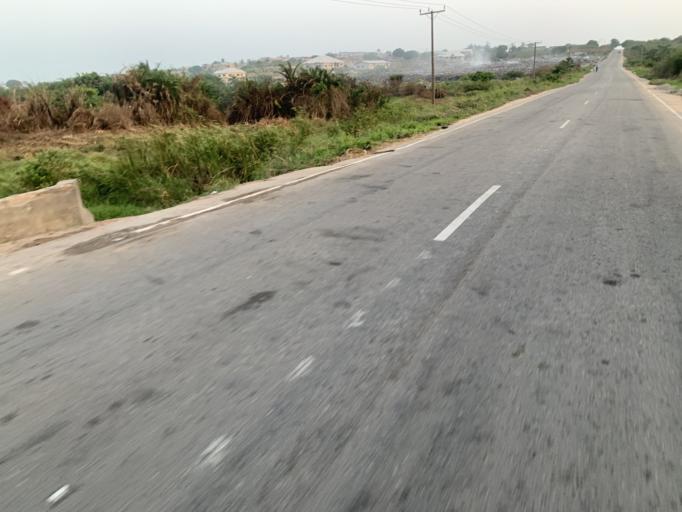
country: GH
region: Central
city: Winneba
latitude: 5.3651
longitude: -0.6085
